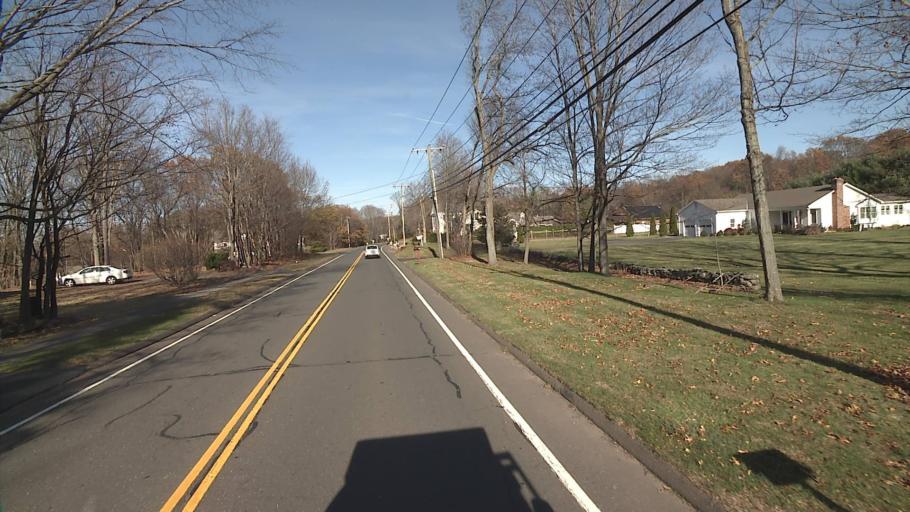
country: US
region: Connecticut
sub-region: Hartford County
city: Glastonbury Center
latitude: 41.6454
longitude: -72.6056
